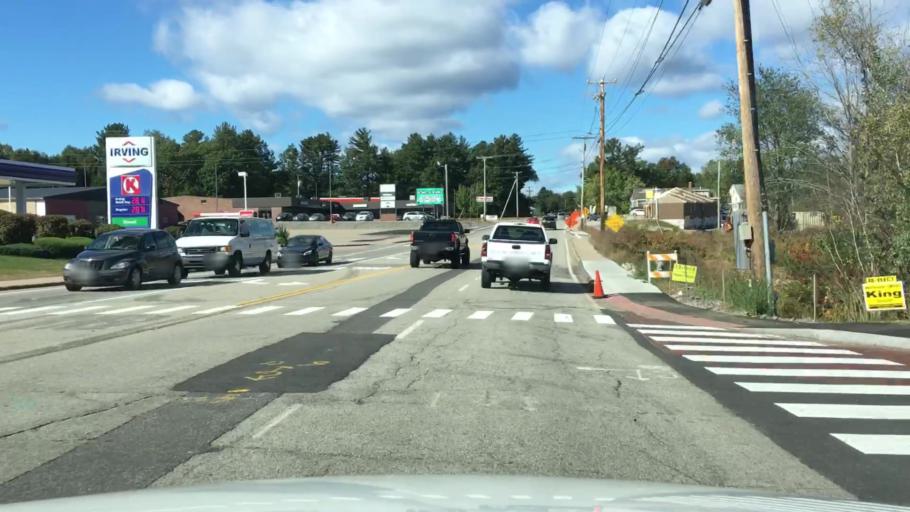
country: US
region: Maine
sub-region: York County
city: South Sanford
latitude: 43.4201
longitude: -70.7567
